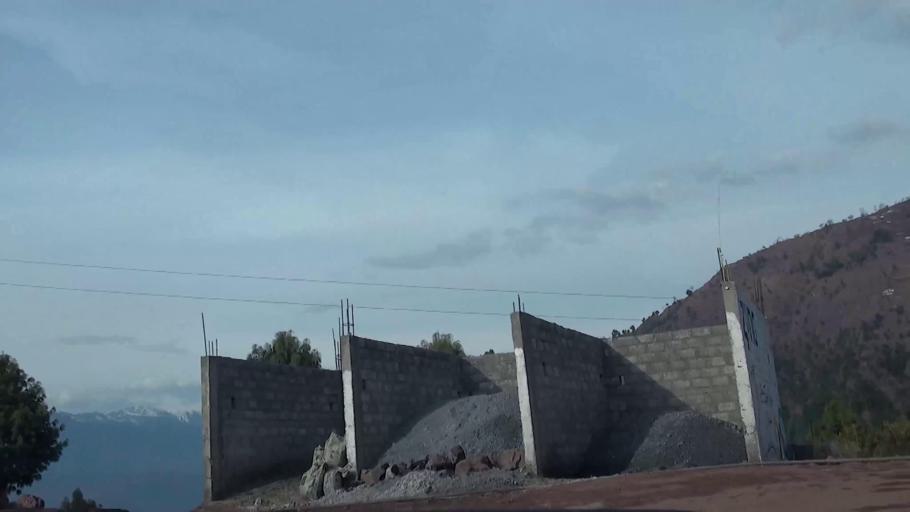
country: PK
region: Azad Kashmir
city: Muzaffarabad
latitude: 34.3689
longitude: 73.5123
